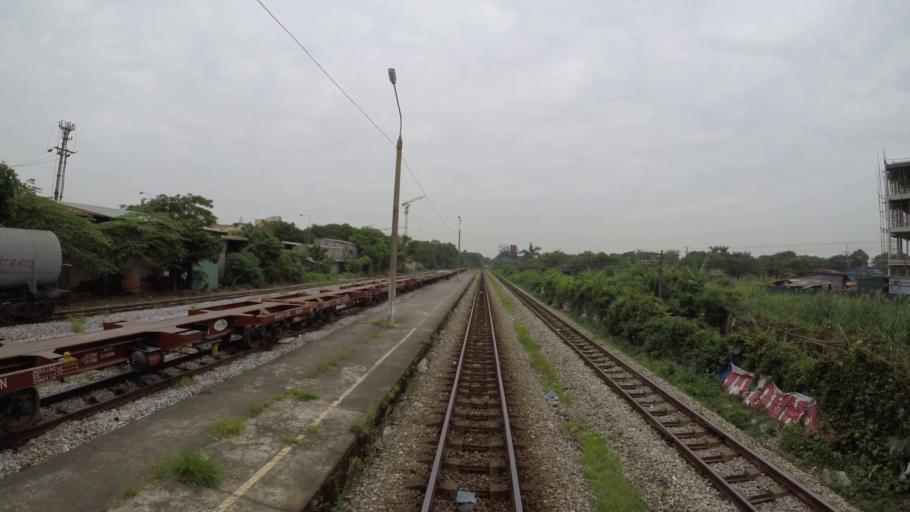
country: VN
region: Hai Phong
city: An Duong
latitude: 20.8832
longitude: 106.6134
